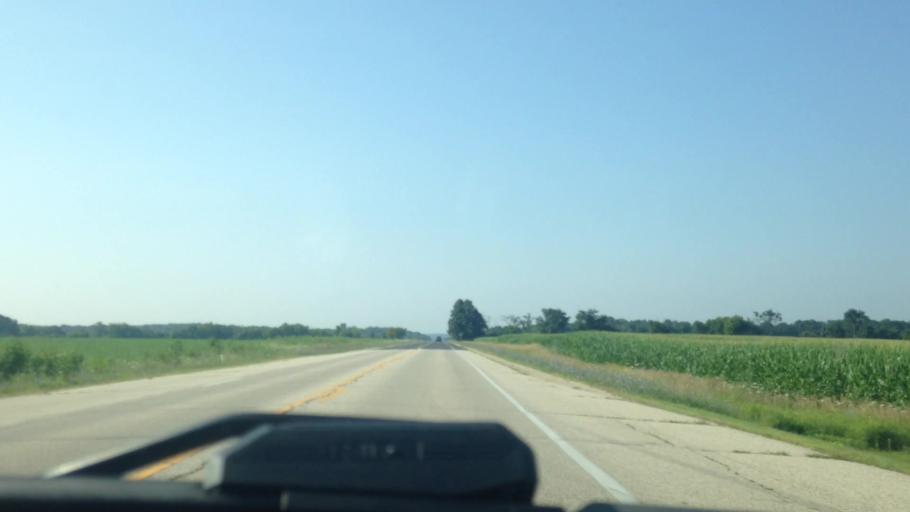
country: US
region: Wisconsin
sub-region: Washington County
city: Richfield
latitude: 43.2187
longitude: -88.2618
